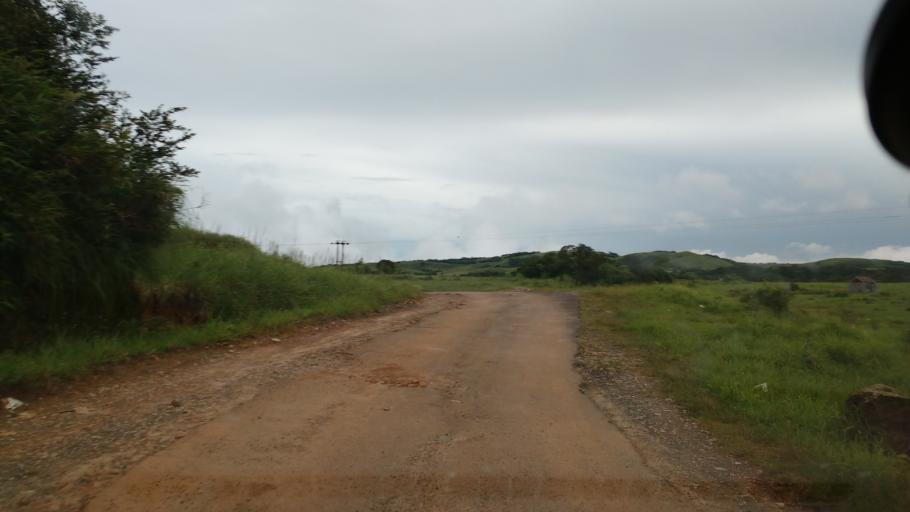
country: IN
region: Meghalaya
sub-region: East Khasi Hills
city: Cherrapunji
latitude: 25.2786
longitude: 91.6939
